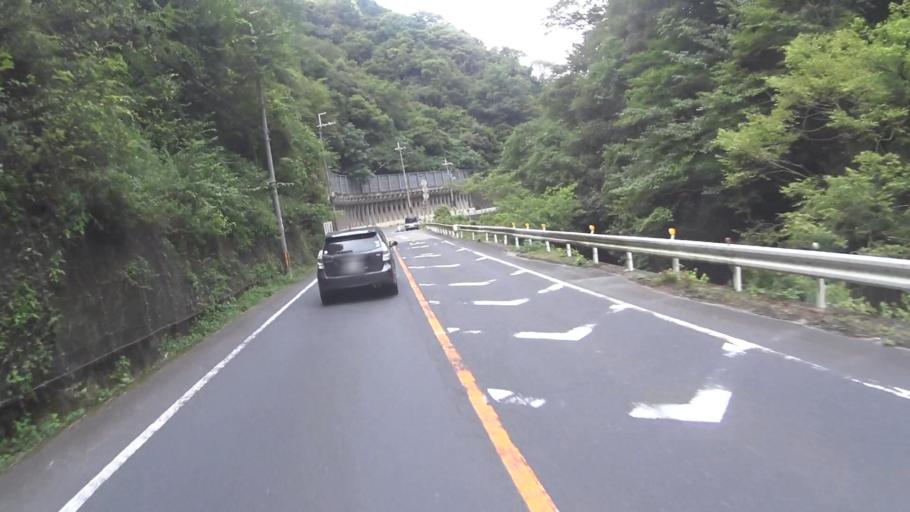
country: JP
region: Kyoto
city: Uji
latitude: 34.8642
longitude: 135.8374
